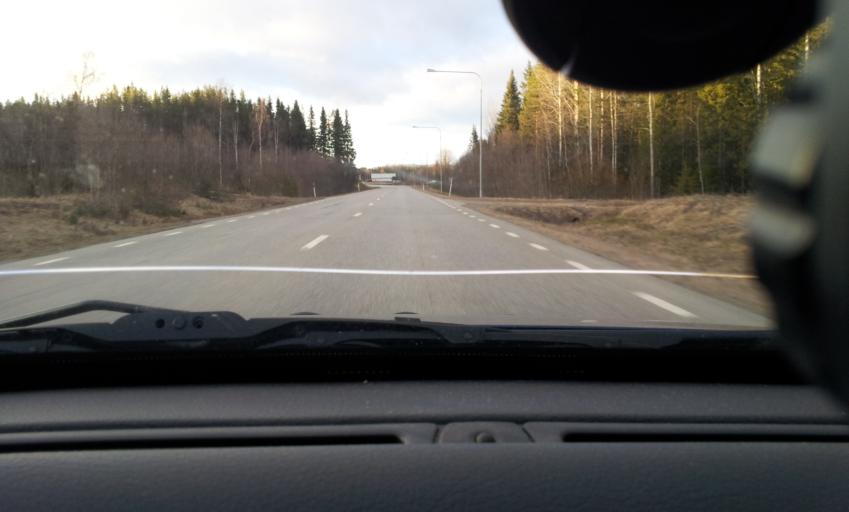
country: SE
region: Jaemtland
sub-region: Bergs Kommun
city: Hoverberg
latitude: 62.7225
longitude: 14.4156
